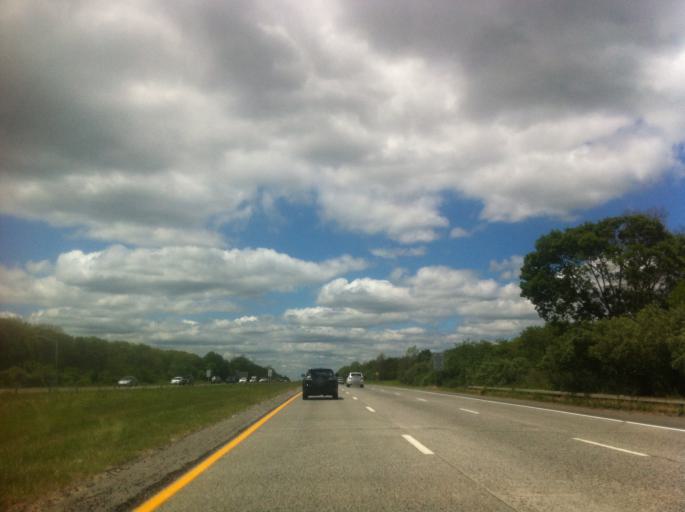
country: US
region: New York
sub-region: Suffolk County
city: Yaphank
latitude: 40.8288
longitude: -72.9398
